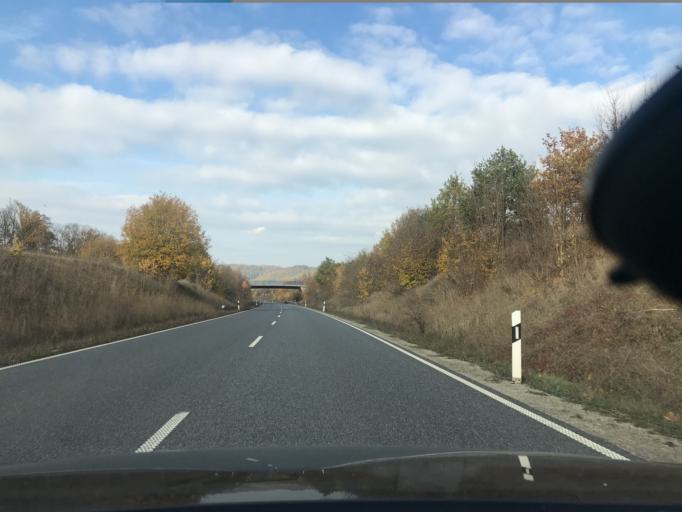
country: DE
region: Hesse
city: Wanfried
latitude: 51.1858
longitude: 10.1798
